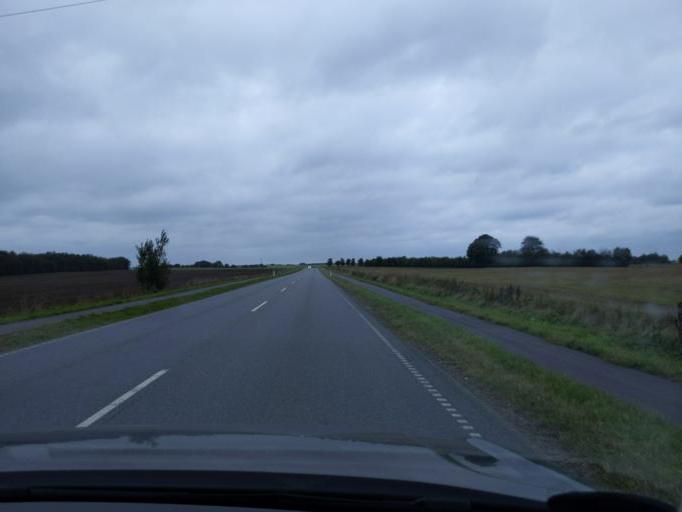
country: DK
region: North Denmark
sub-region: Mariagerfjord Kommune
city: Hobro
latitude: 56.6011
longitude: 9.7985
